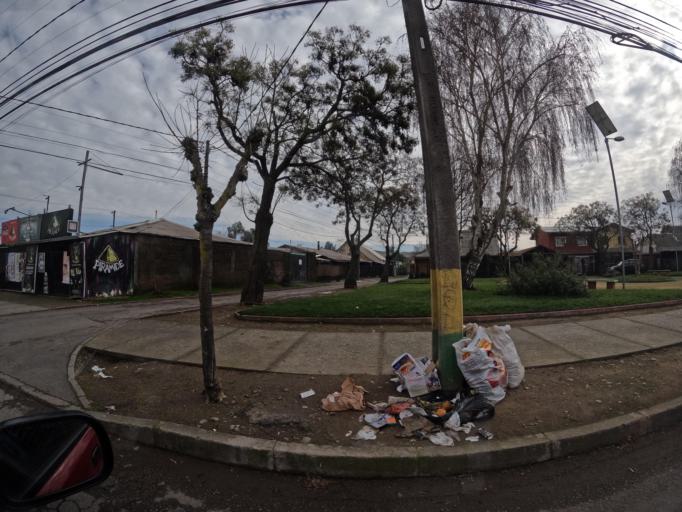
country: CL
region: Maule
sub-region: Provincia de Linares
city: Linares
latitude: -35.8360
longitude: -71.6020
